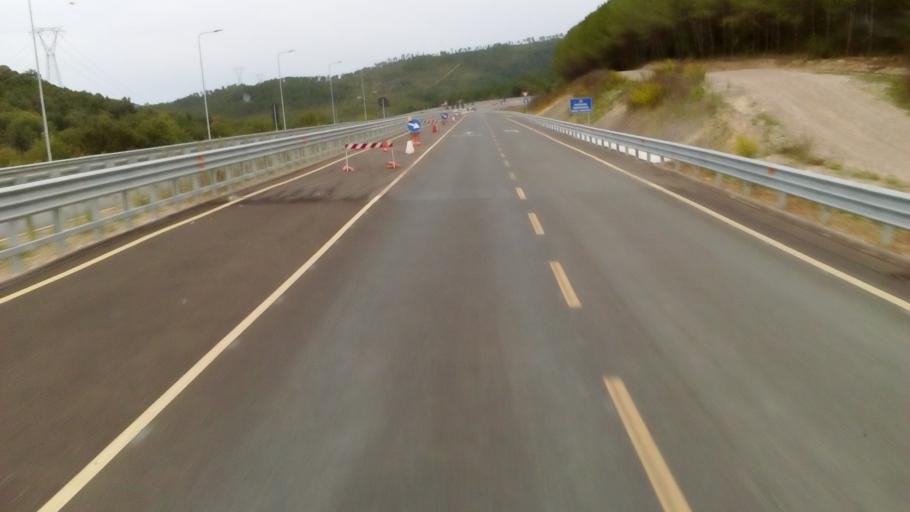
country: IT
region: Tuscany
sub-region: Provincia di Grosseto
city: Civitella Marittima
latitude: 43.0299
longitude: 11.2776
